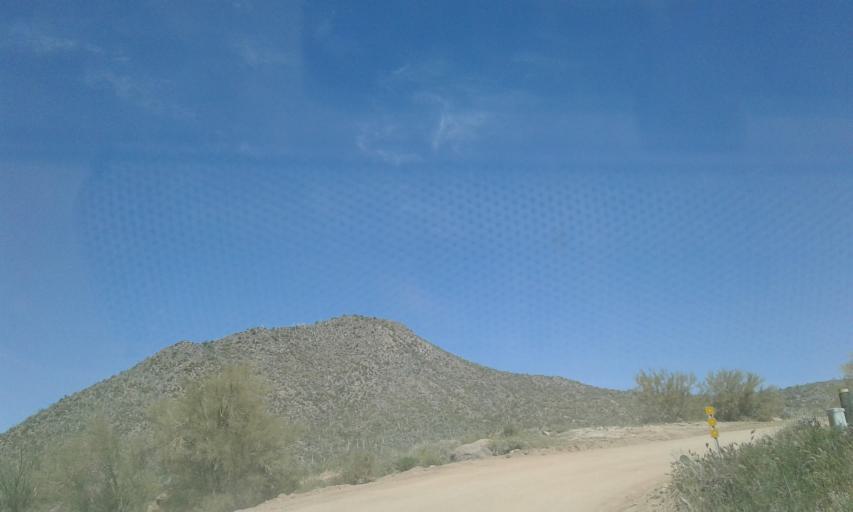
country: US
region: Arizona
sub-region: Gila County
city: Tonto Basin
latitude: 33.6014
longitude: -111.2043
